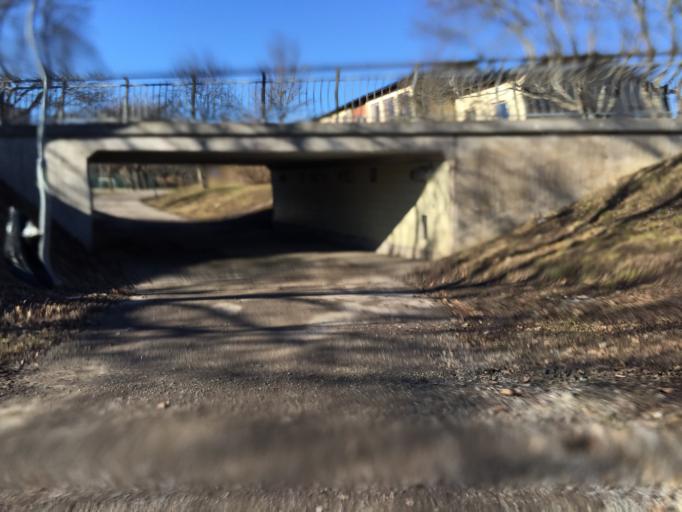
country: SE
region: Stockholm
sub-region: Stockholms Kommun
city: Bromma
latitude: 59.3623
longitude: 17.8831
